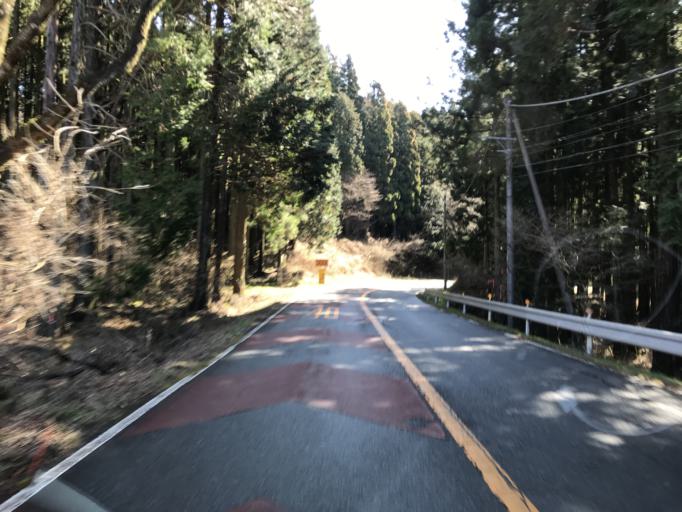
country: JP
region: Shizuoka
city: Fujinomiya
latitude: 35.2923
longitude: 138.6634
